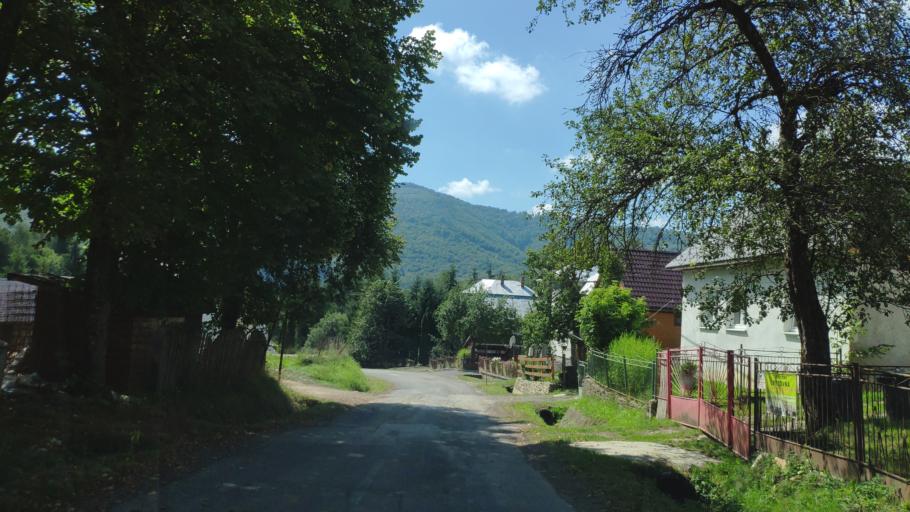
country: PL
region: Subcarpathian Voivodeship
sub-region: Powiat leski
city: Cisna
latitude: 49.0708
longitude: 22.4003
